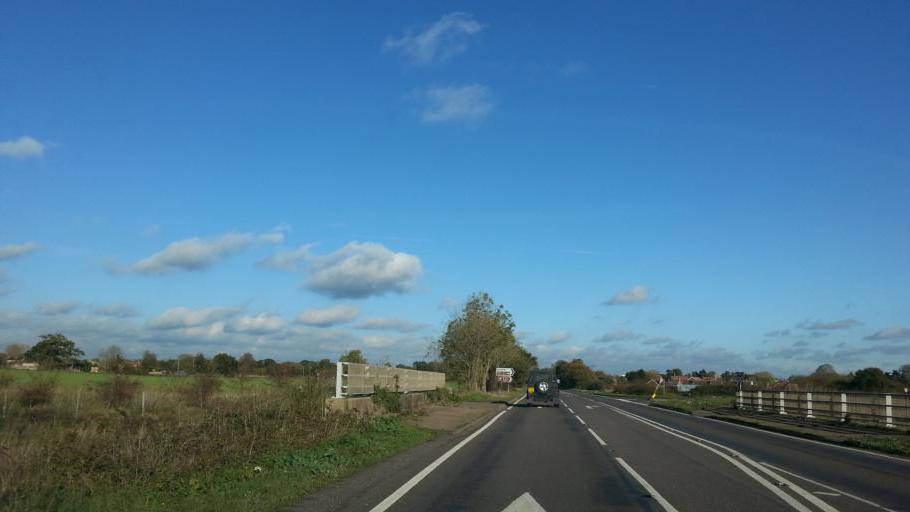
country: GB
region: England
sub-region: Suffolk
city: Bungay
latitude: 52.4483
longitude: 1.4089
